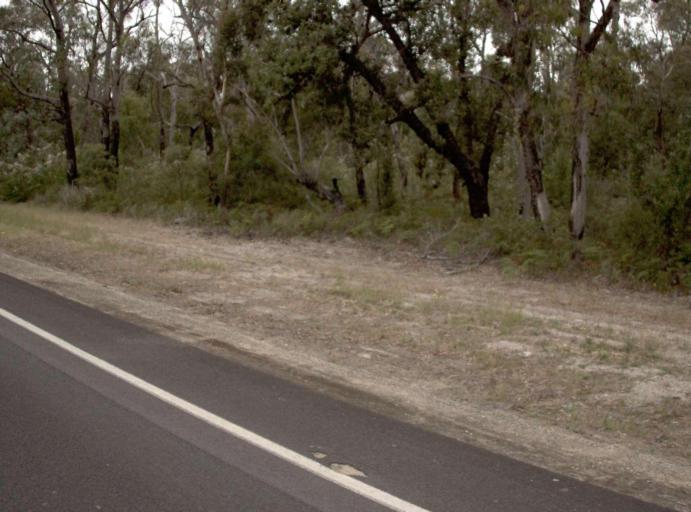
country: AU
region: Victoria
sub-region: Wellington
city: Sale
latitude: -38.3189
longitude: 147.0234
